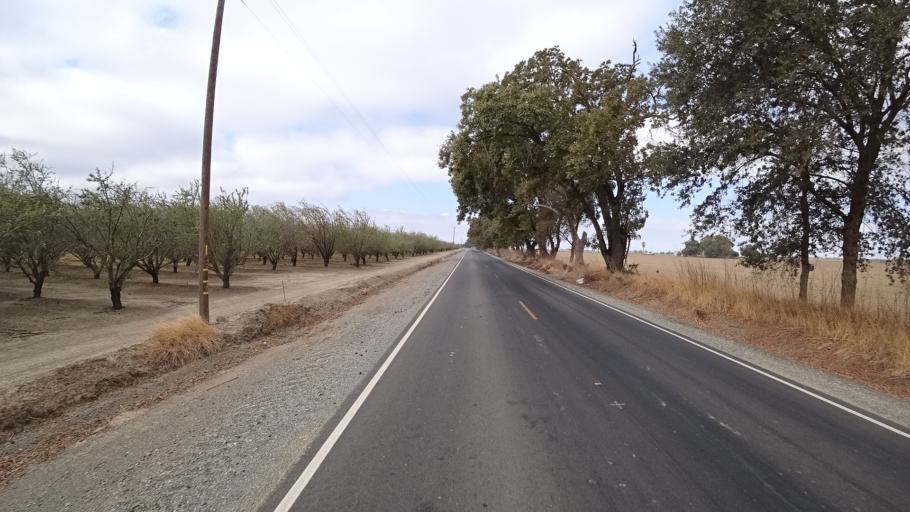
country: US
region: California
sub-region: Yolo County
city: Woodland
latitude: 38.7935
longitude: -121.8145
